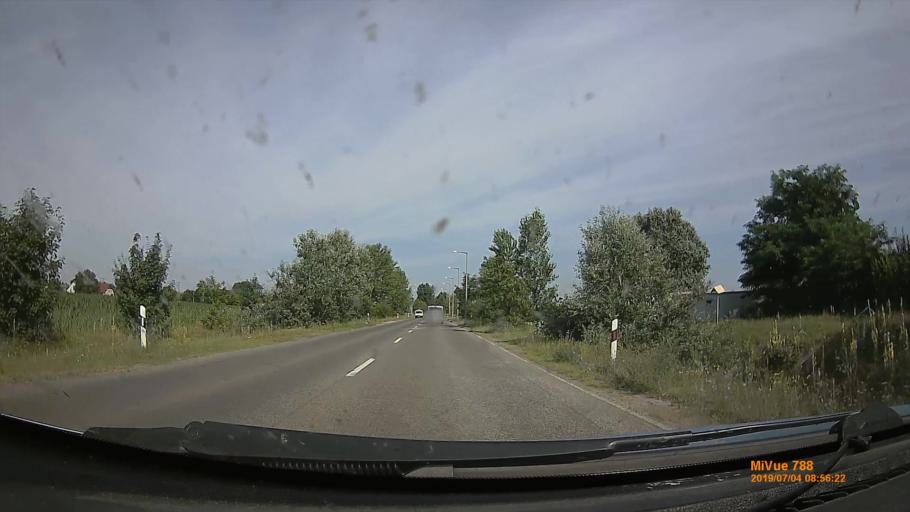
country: HU
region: Pest
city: Gyal
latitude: 47.3877
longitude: 19.2441
